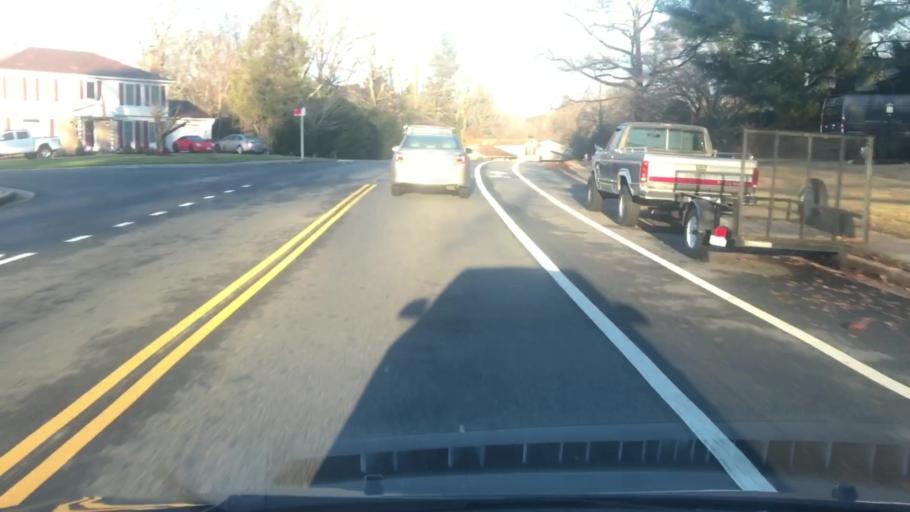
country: US
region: Virginia
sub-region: Fairfax County
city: Kings Park
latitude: 38.8207
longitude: -77.2380
